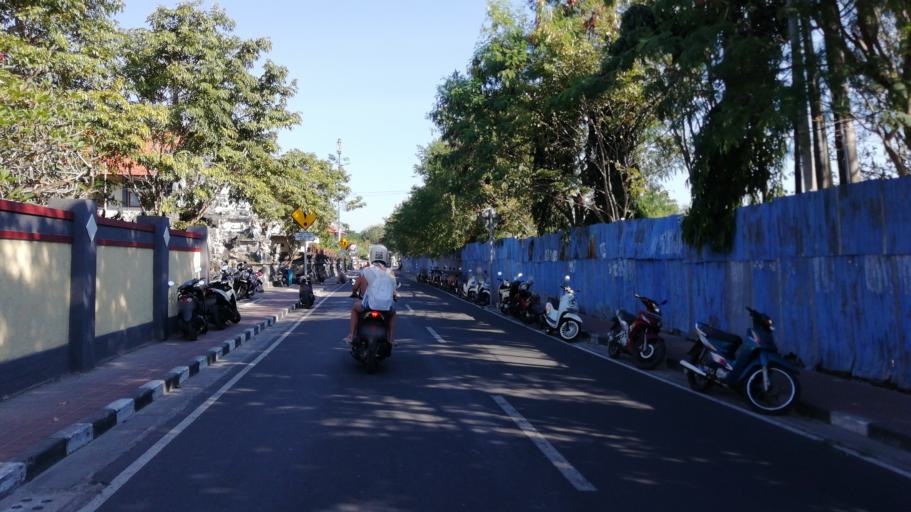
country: ID
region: Bali
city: Bualu
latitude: -8.7606
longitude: 115.2219
